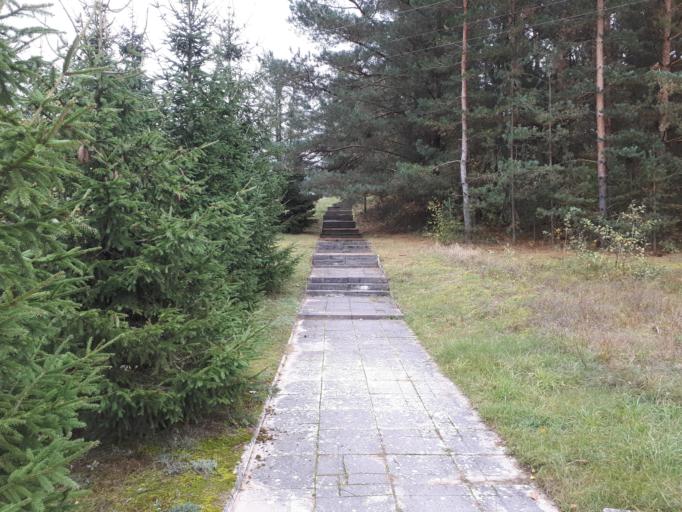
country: LT
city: Kalvarija
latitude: 54.3883
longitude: 23.2175
